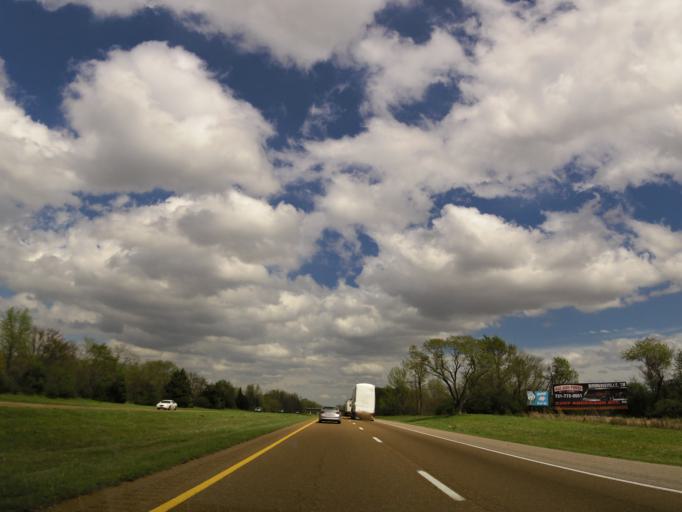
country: US
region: Tennessee
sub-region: Tipton County
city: Mason
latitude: 35.3787
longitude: -89.4462
